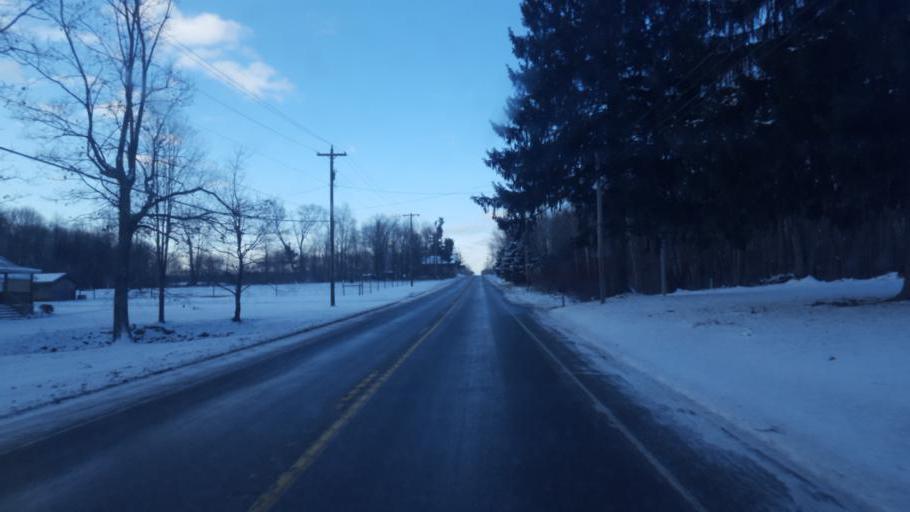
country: US
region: Pennsylvania
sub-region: Mercer County
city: Stoneboro
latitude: 41.3854
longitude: -80.2175
